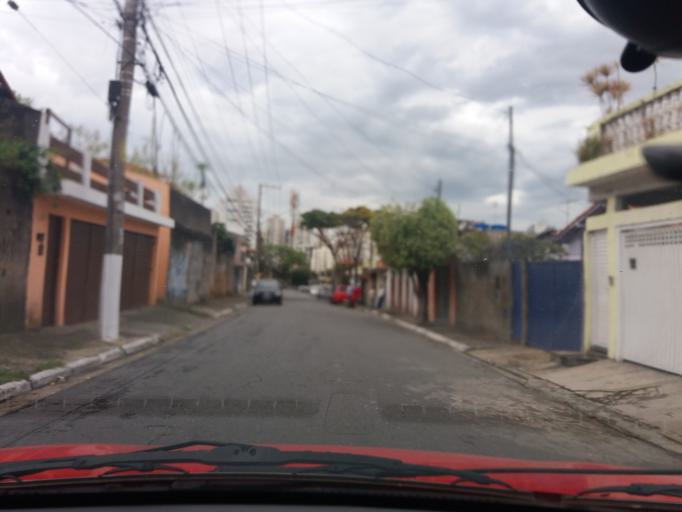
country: BR
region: Sao Paulo
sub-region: Taboao Da Serra
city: Taboao da Serra
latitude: -23.6144
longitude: -46.7457
